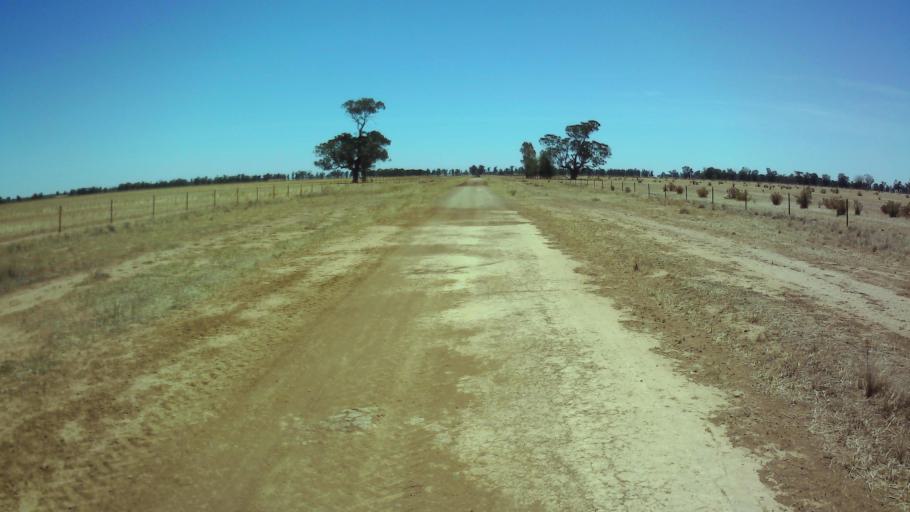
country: AU
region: New South Wales
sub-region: Weddin
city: Grenfell
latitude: -33.9873
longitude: 147.7349
